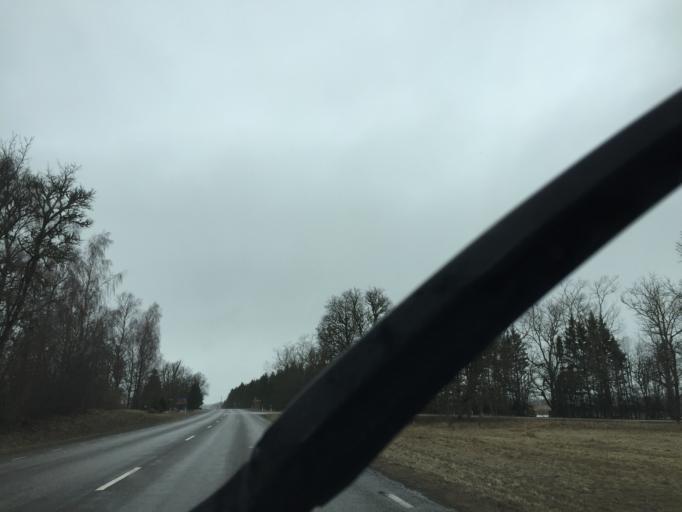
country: EE
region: Laeaene
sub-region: Ridala Parish
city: Uuemoisa
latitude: 58.8779
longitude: 23.6085
